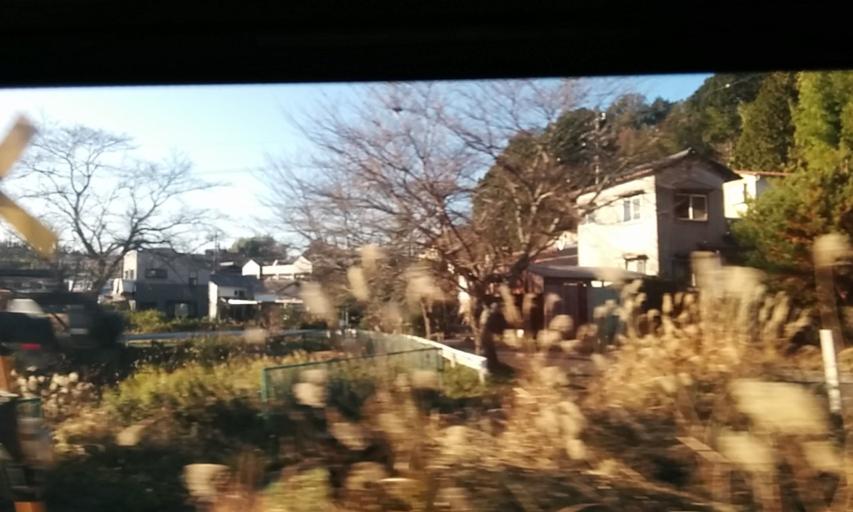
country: JP
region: Gifu
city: Nakatsugawa
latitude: 35.5056
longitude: 137.5054
